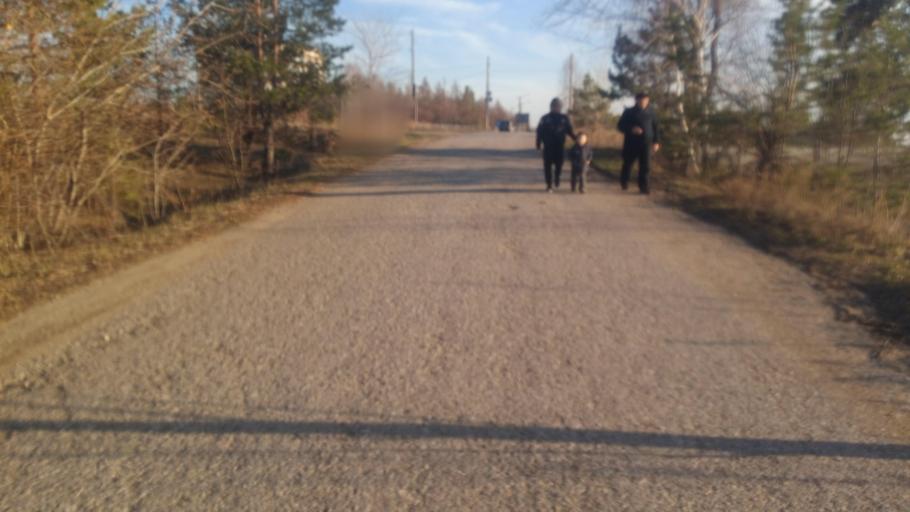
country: RU
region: Chelyabinsk
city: Novosineglazovskiy
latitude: 55.1259
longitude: 61.3289
